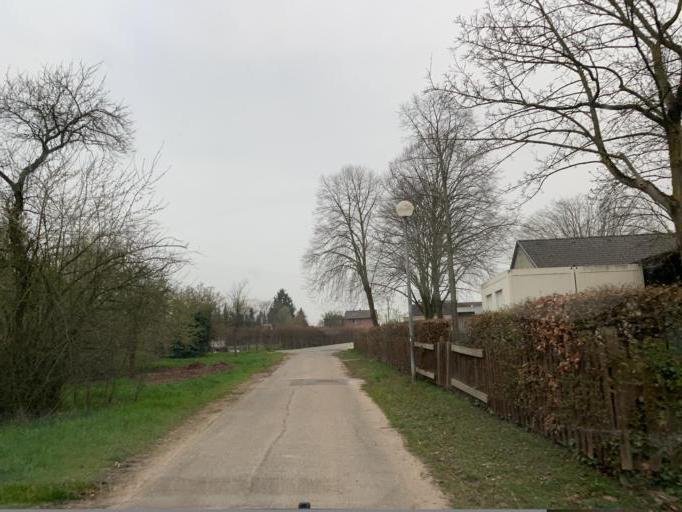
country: DE
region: North Rhine-Westphalia
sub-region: Regierungsbezirk Koln
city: Elsdorf
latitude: 50.8843
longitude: 6.5992
